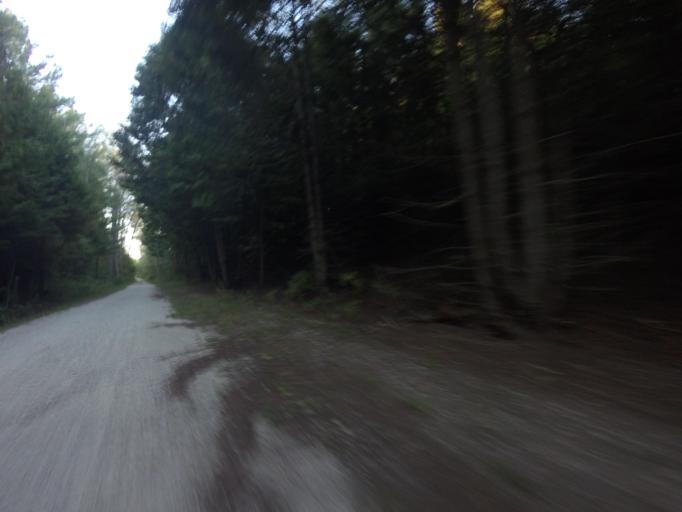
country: CA
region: Ontario
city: Brampton
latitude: 43.9207
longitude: -79.8416
